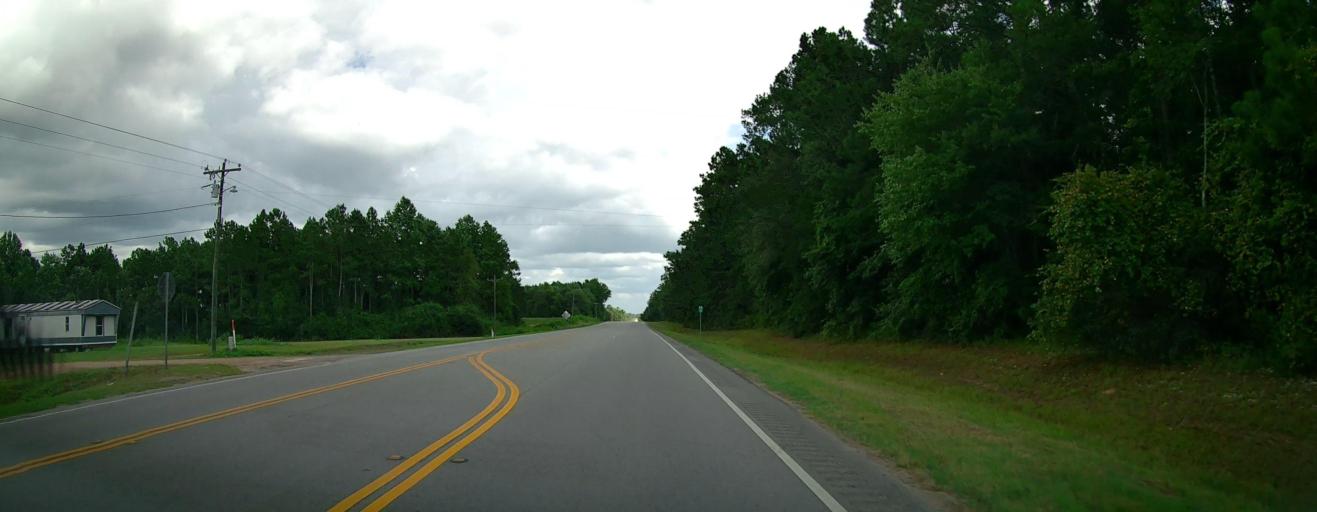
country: US
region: Georgia
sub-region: Coffee County
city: Broxton
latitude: 31.5677
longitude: -83.0116
